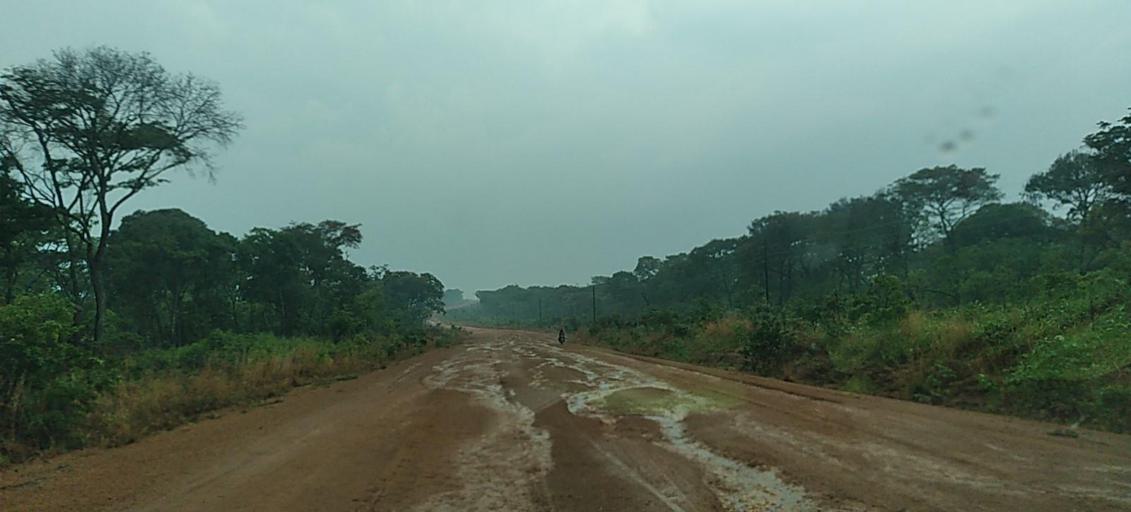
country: ZM
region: North-Western
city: Mwinilunga
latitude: -11.5928
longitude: 24.3891
